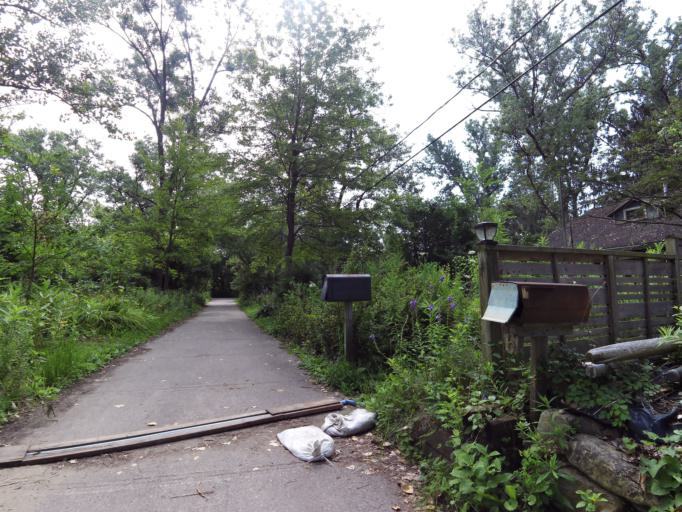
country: CA
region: Ontario
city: Toronto
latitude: 43.6330
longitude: -79.3538
